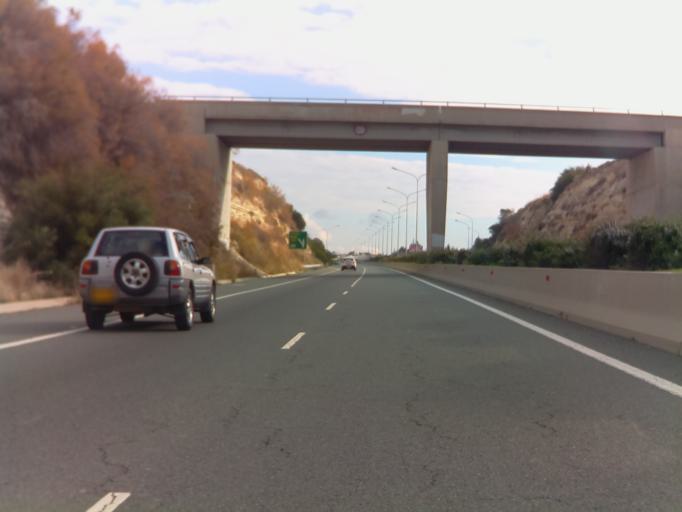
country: CY
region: Limassol
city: Erimi
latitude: 34.6862
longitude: 32.9146
